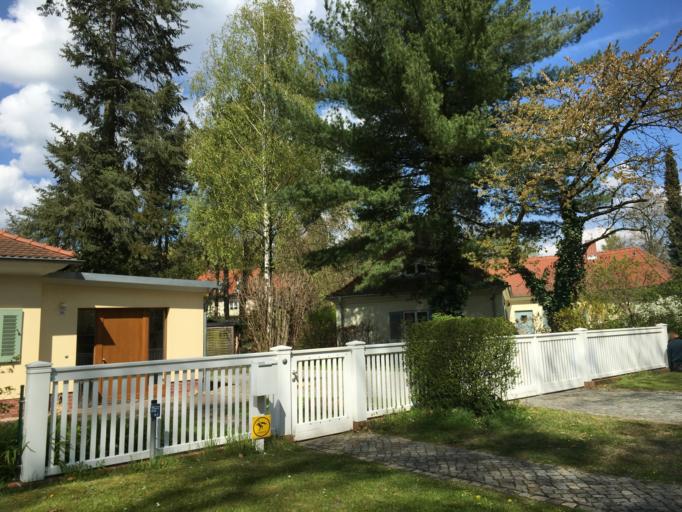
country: DE
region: Brandenburg
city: Potsdam
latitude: 52.4207
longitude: 13.0684
